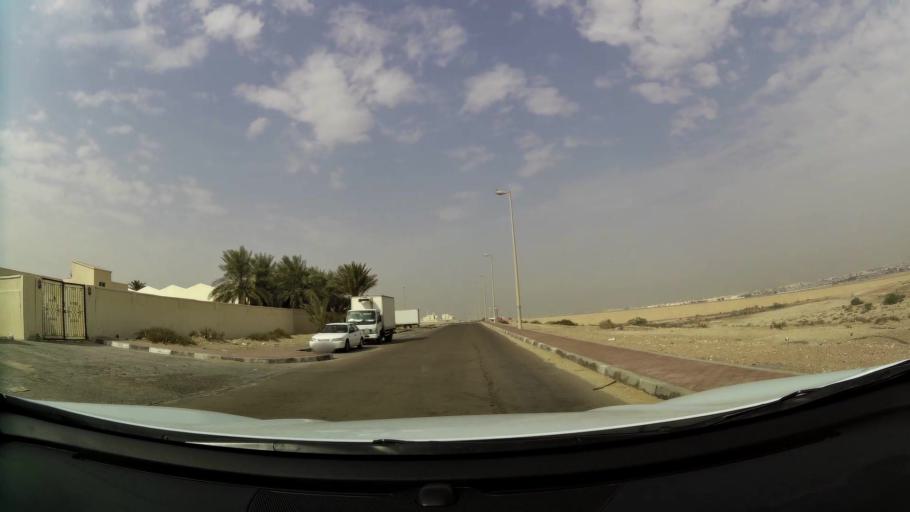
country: AE
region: Abu Dhabi
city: Abu Dhabi
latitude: 24.2755
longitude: 54.6728
